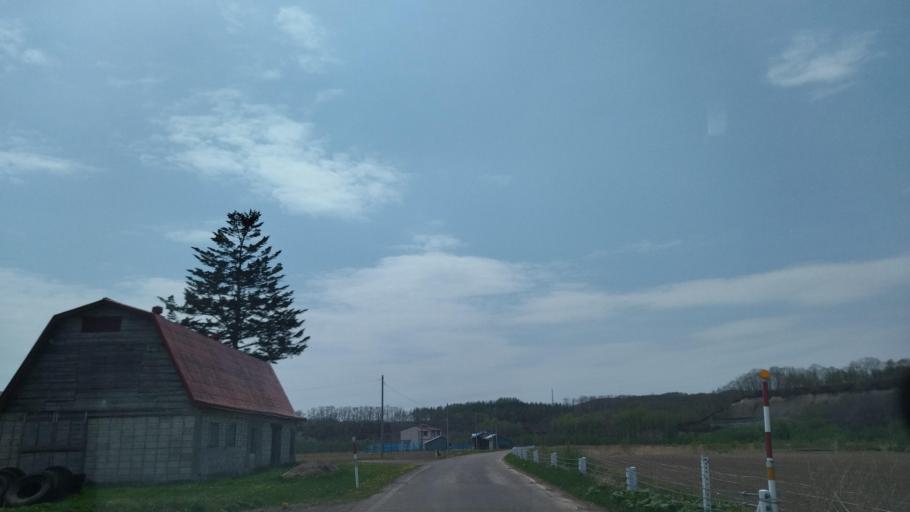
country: JP
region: Hokkaido
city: Otofuke
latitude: 43.3174
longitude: 143.5746
